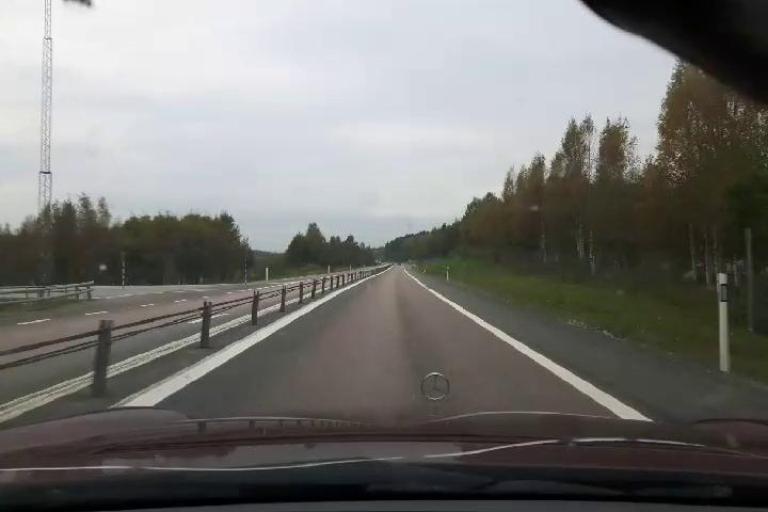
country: SE
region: Vaesternorrland
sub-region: Haernoesands Kommun
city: Haernoesand
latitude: 62.8551
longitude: 18.0150
